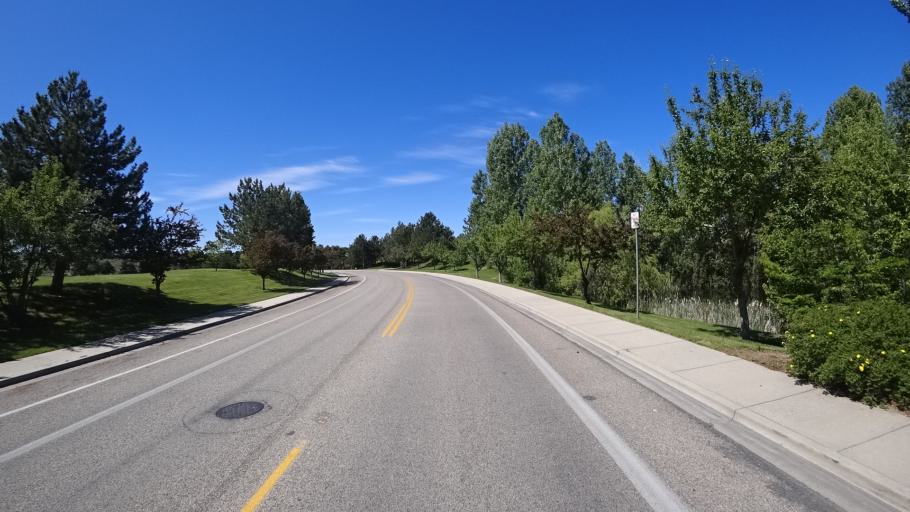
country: US
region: Idaho
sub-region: Ada County
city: Boise
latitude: 43.5501
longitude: -116.1524
